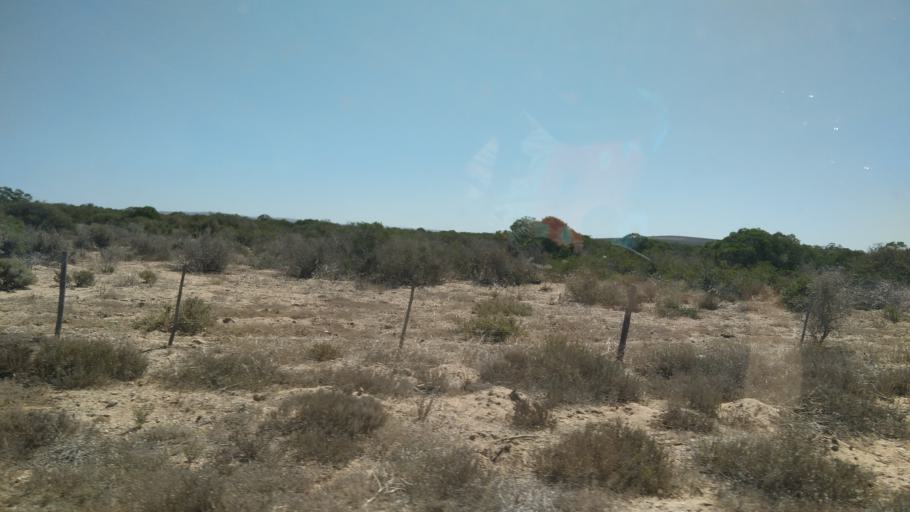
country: ZA
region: Western Cape
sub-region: West Coast District Municipality
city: Vredenburg
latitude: -32.9975
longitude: 18.1291
